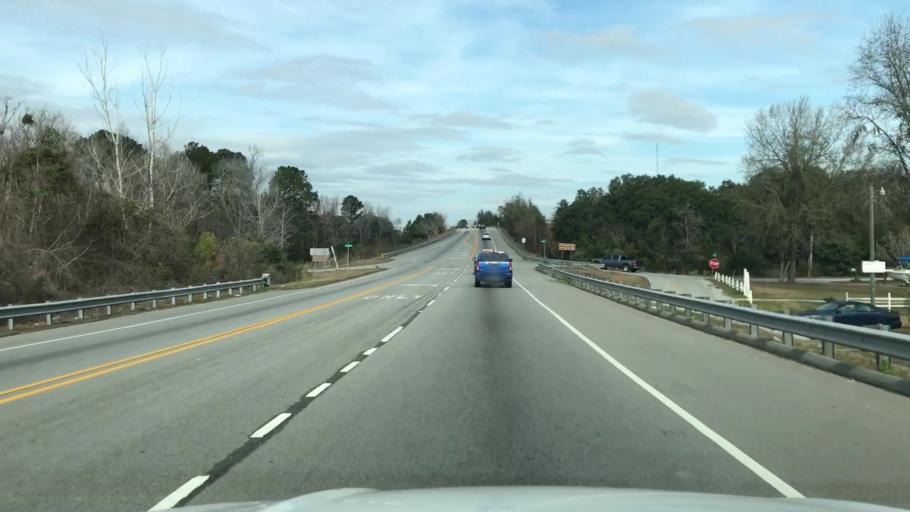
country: US
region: South Carolina
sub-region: Charleston County
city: Shell Point
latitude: 32.7898
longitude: -80.1080
